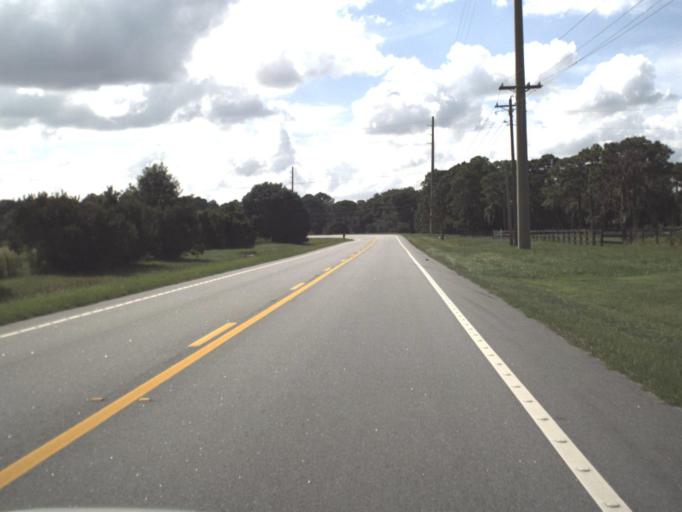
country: US
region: Florida
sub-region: Hardee County
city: Wauchula
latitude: 27.4705
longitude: -82.0686
